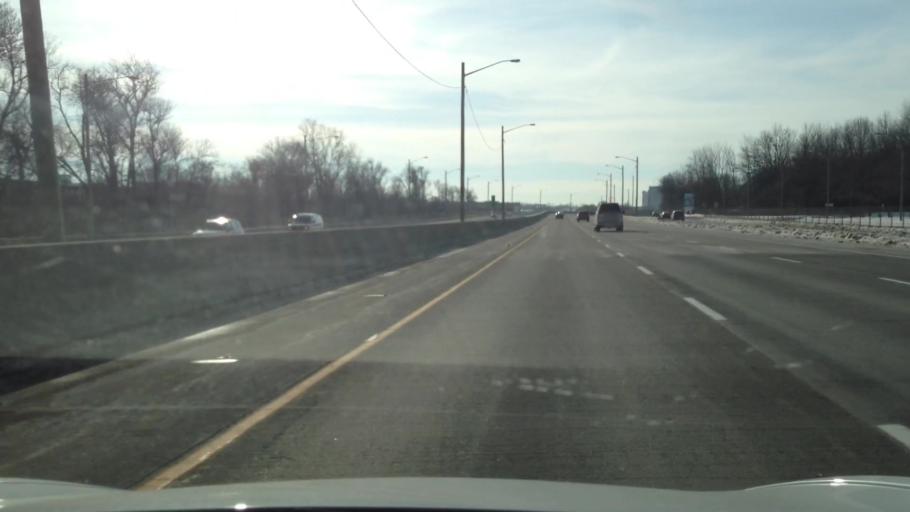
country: CA
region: Quebec
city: Baie-D'Urfe
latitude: 45.4230
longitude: -73.9251
